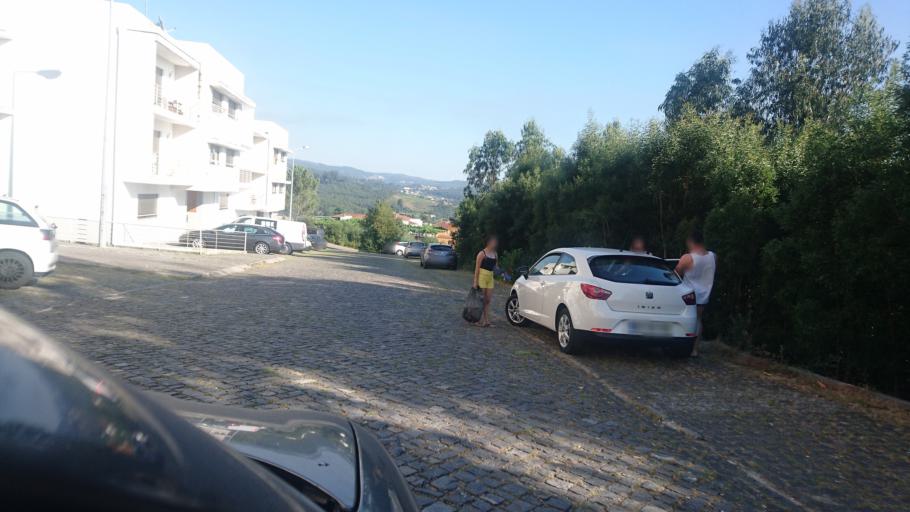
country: PT
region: Porto
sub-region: Paredes
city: Recarei
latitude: 41.1517
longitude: -8.3916
